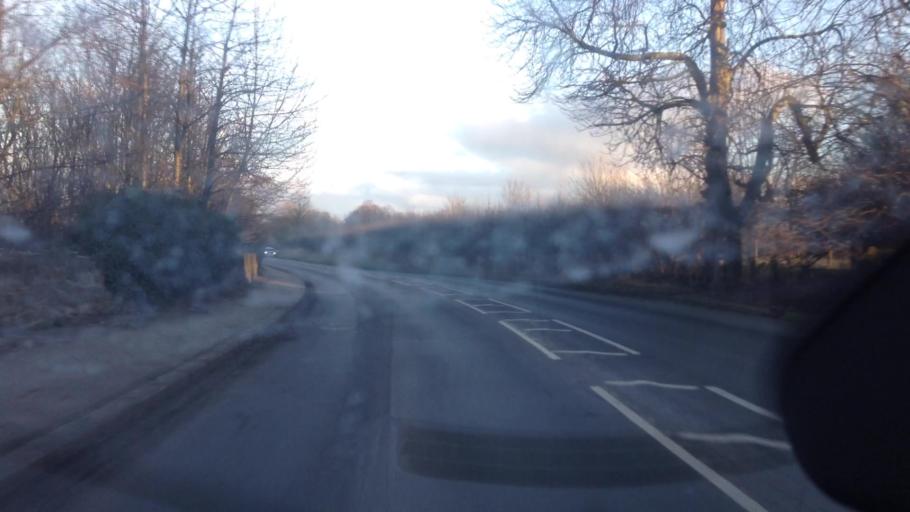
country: GB
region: England
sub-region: City and Borough of Leeds
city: Pool
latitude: 53.9054
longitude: -1.6522
